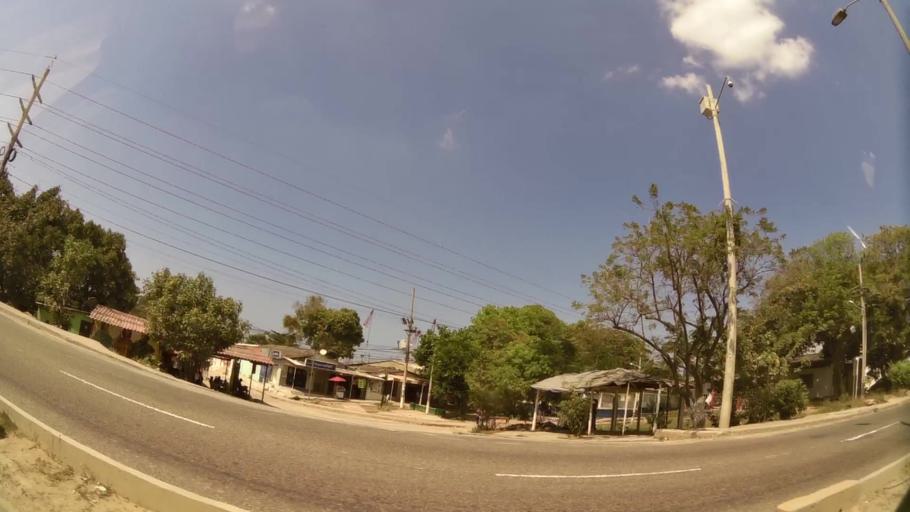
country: CO
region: Bolivar
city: Cartagena
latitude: 10.3686
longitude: -75.5072
